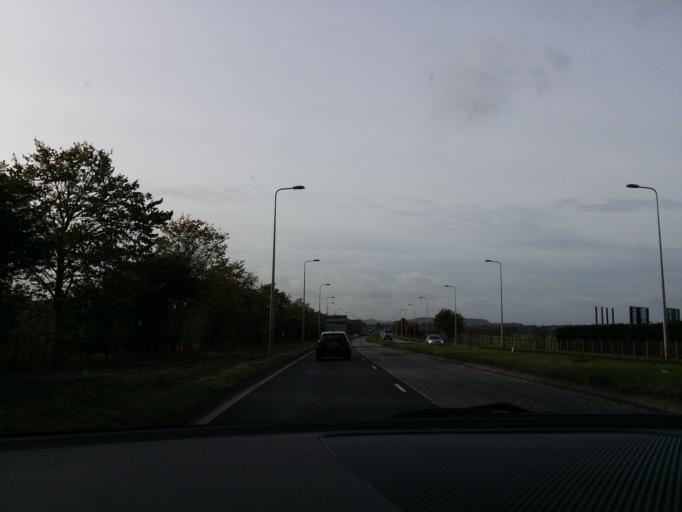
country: GB
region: Scotland
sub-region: Edinburgh
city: Ratho
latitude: 55.9384
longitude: -3.3790
